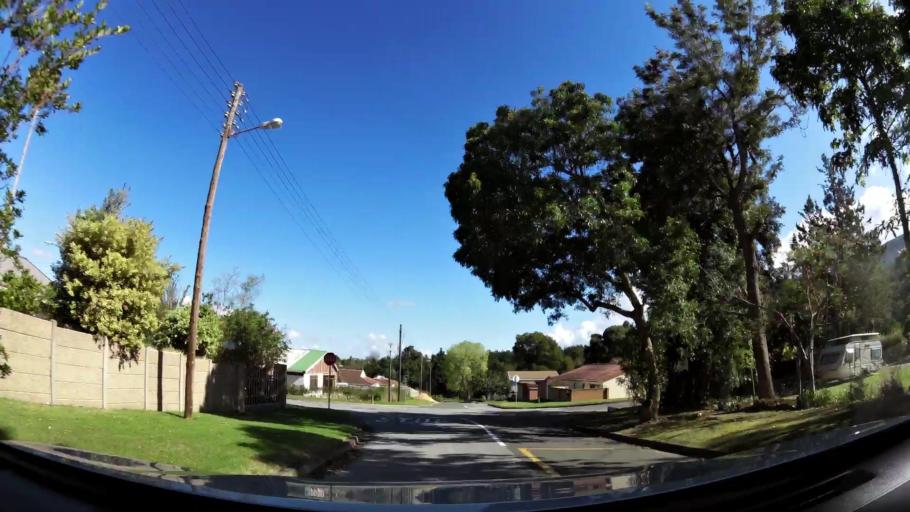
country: ZA
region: Western Cape
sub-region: Eden District Municipality
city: George
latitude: -33.9400
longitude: 22.4720
